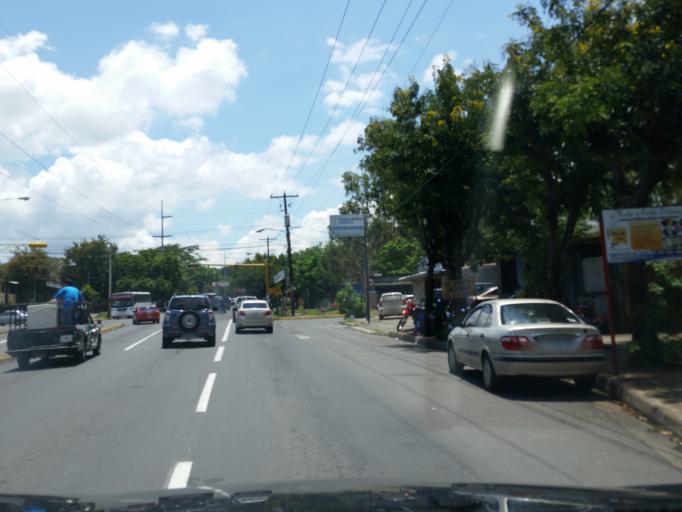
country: NI
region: Managua
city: Managua
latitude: 12.1207
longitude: -86.2738
